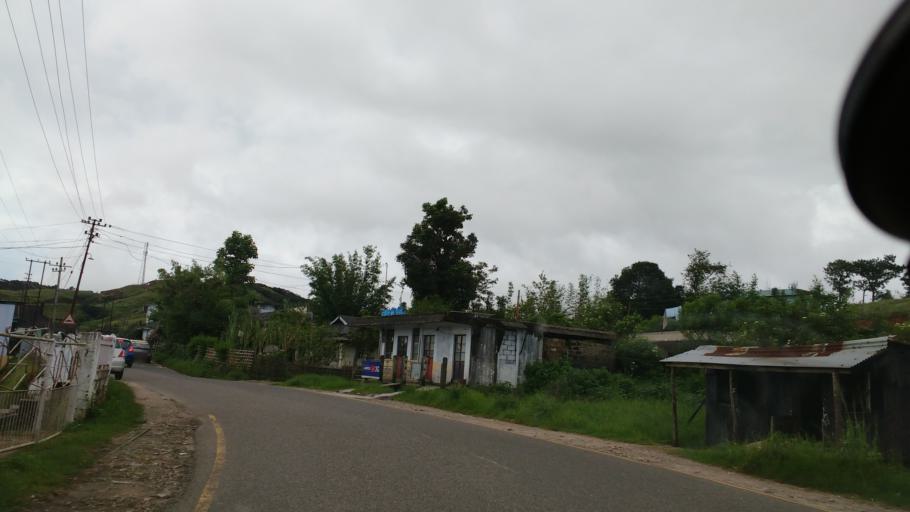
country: IN
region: Meghalaya
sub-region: East Khasi Hills
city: Cherrapunji
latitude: 25.2747
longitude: 91.7317
